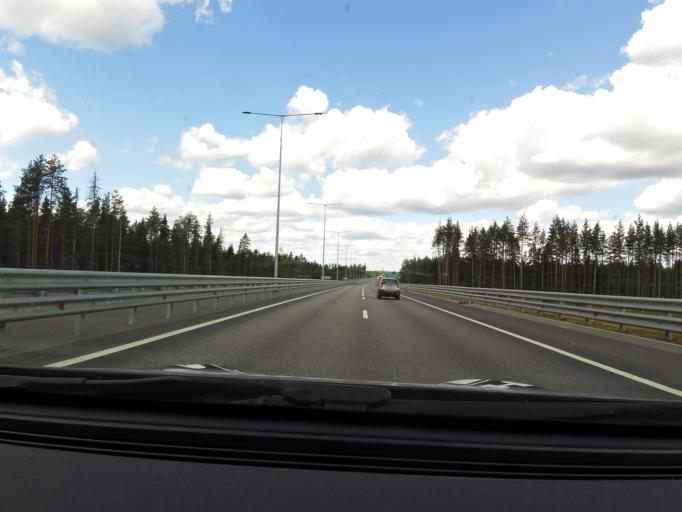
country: RU
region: Tverskaya
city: Krasnomayskiy
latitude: 57.4808
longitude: 34.3280
